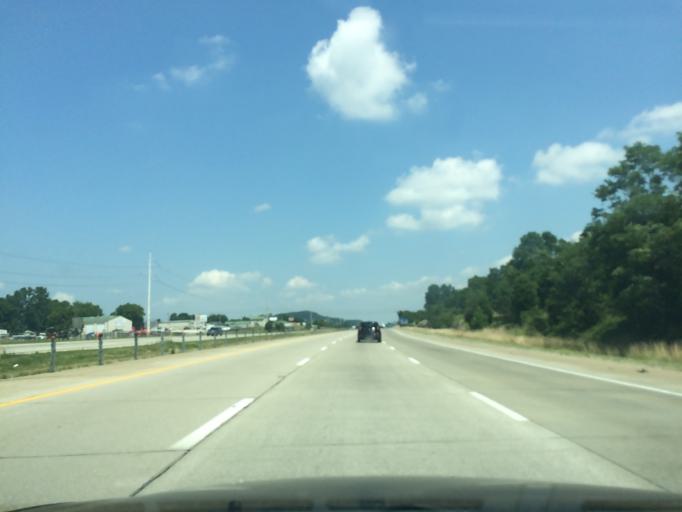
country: US
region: Kentucky
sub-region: Bullitt County
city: Brooks
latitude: 38.0485
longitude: -85.6980
